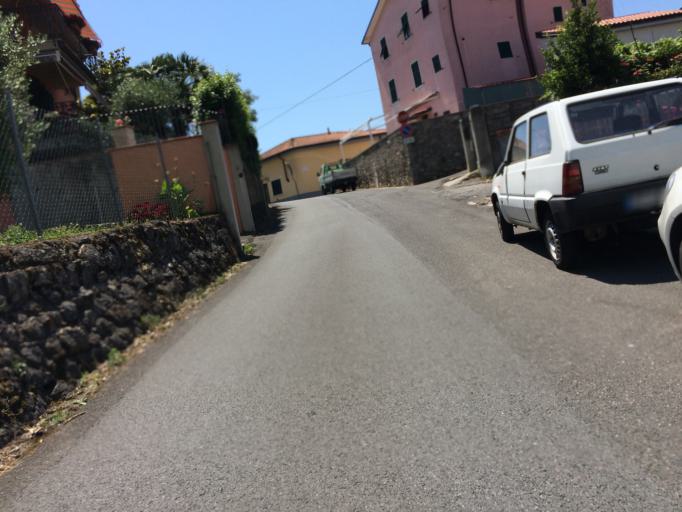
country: IT
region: Tuscany
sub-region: Provincia di Massa-Carrara
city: Carrara
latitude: 44.0771
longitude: 10.1109
